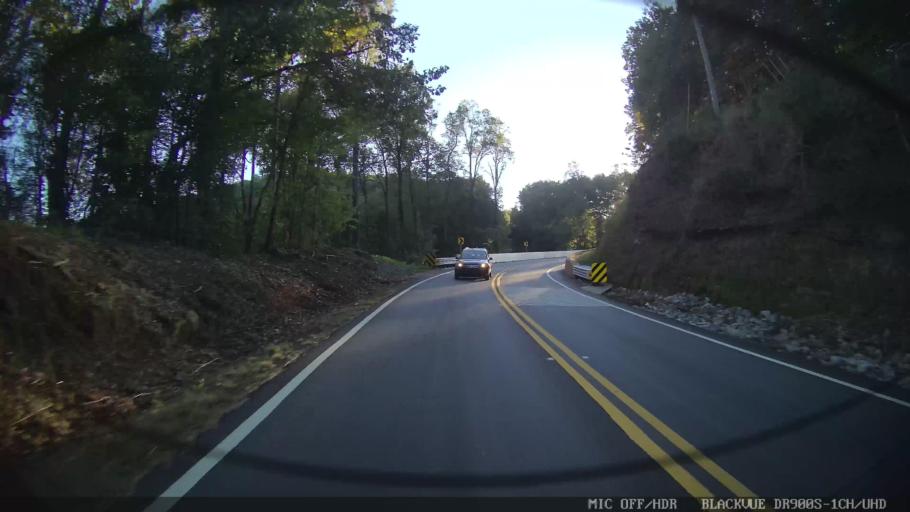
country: US
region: Georgia
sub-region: Lumpkin County
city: Dahlonega
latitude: 34.6275
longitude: -83.9531
